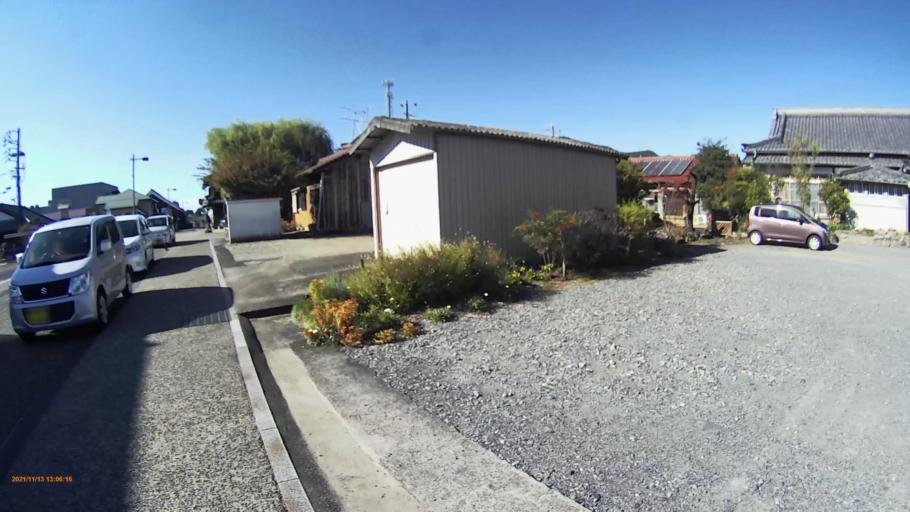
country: JP
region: Gifu
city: Inuyama
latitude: 35.4045
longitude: 136.9381
